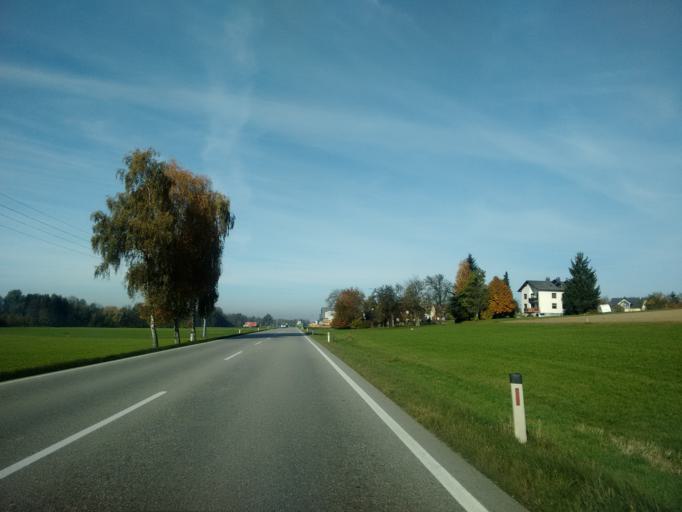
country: AT
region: Upper Austria
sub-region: Politischer Bezirk Ried im Innkreis
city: Ried im Innkreis
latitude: 48.1980
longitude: 13.5432
